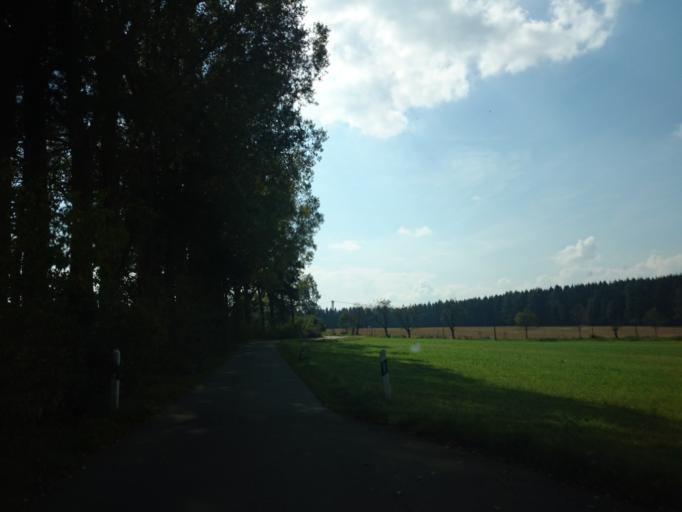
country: DE
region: Saxony
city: Brand-Erbisdorf
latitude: 50.8638
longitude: 13.2884
